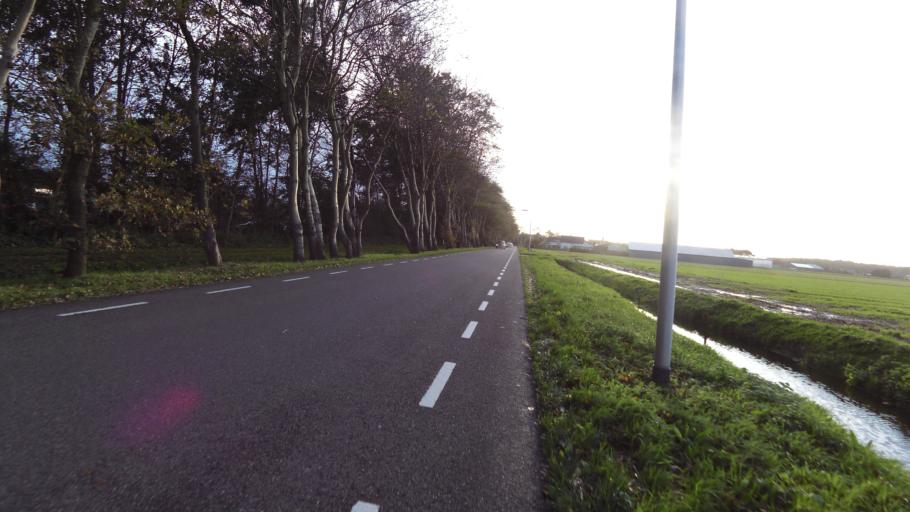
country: NL
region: South Holland
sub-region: Gemeente Noordwijkerhout
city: Noordwijkerhout
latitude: 52.2825
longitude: 4.5006
